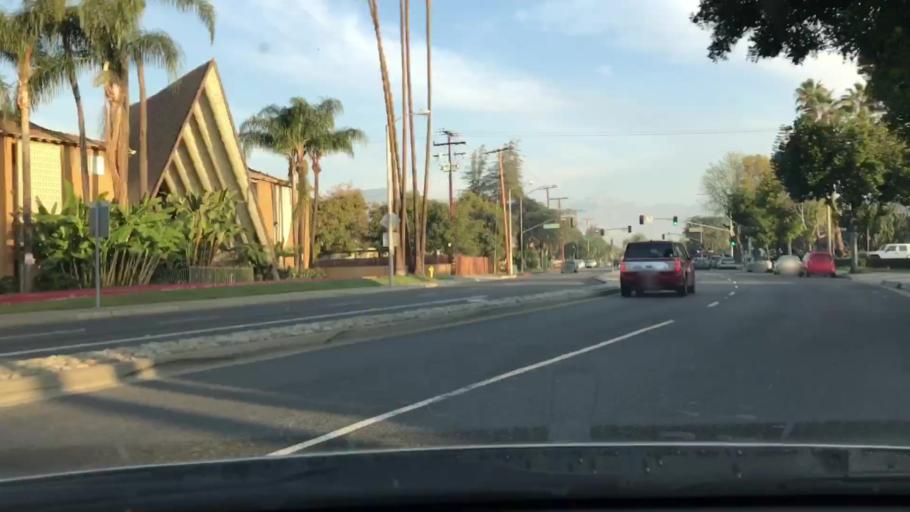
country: US
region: California
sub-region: Los Angeles County
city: West Covina
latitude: 34.0739
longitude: -117.9355
